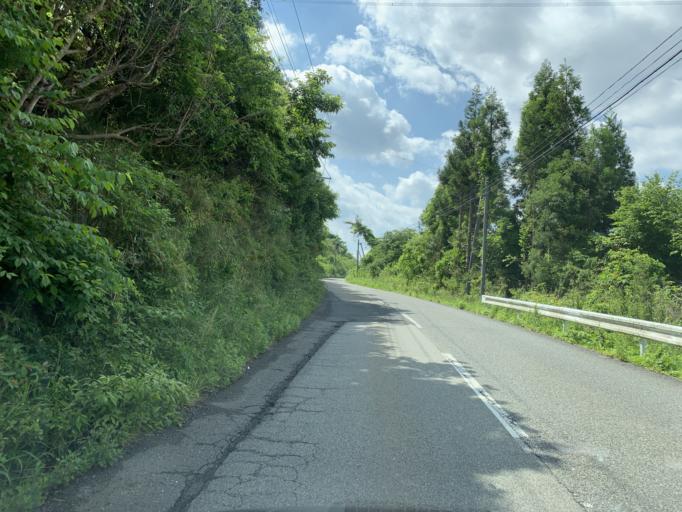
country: JP
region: Miyagi
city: Furukawa
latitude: 38.7779
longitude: 140.9591
